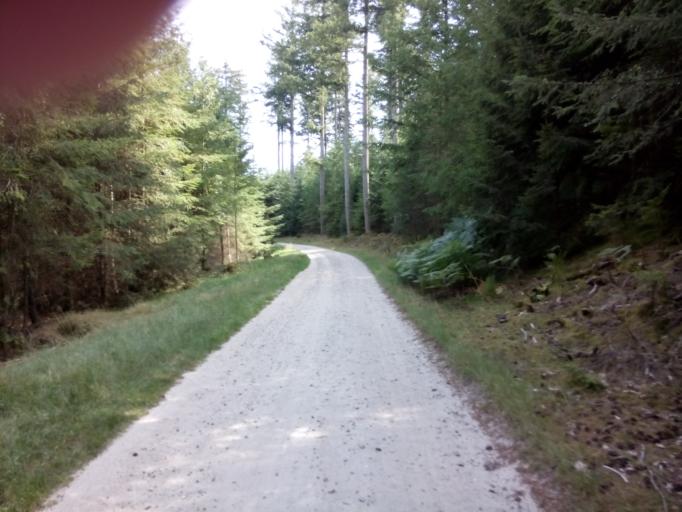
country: DK
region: Central Jutland
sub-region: Skanderborg Kommune
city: Ry
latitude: 56.0918
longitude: 9.7212
